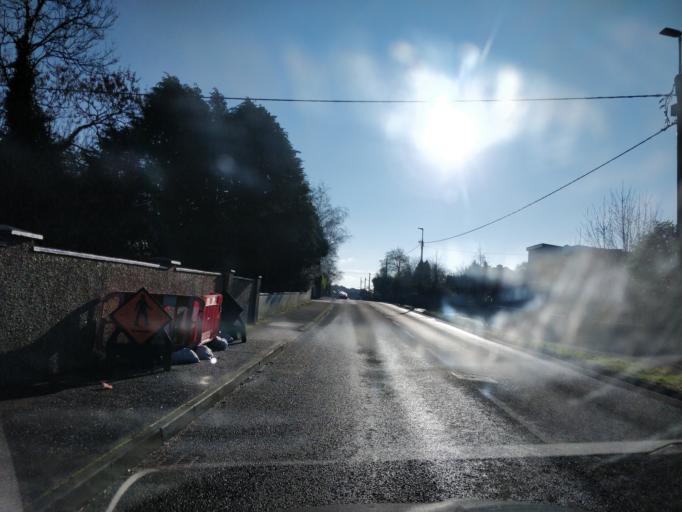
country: IE
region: Connaught
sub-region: County Galway
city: Bearna
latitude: 53.2665
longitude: -9.1064
